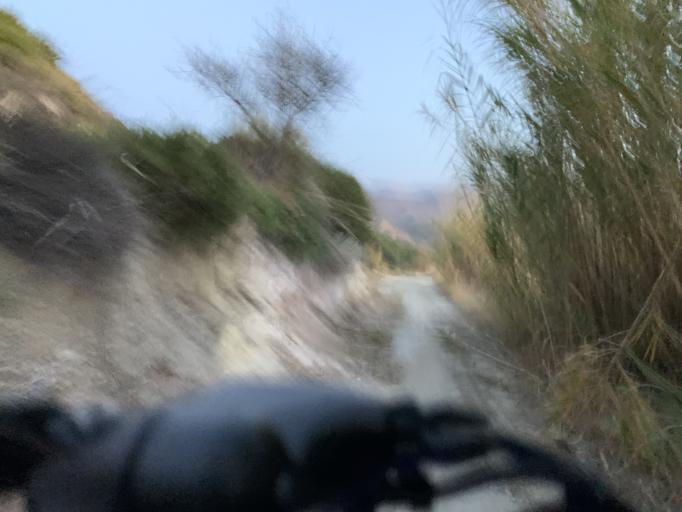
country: ES
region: Andalusia
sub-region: Provincia de Granada
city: Beas de Granada
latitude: 37.2205
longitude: -3.4531
